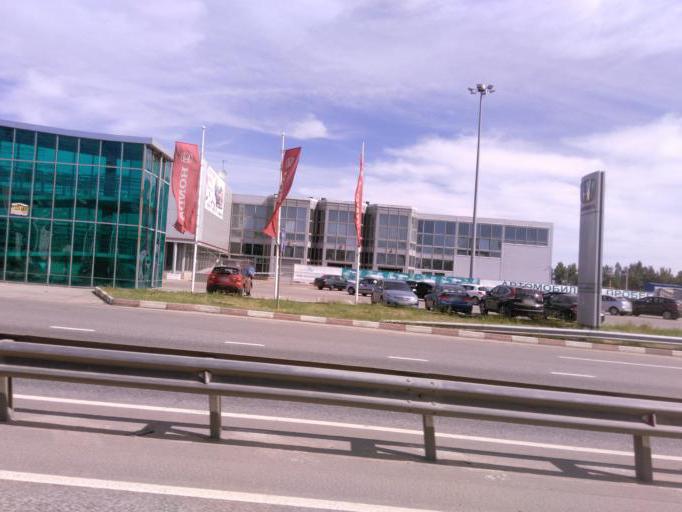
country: RU
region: Moskovskaya
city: Skhodnya
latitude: 55.9744
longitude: 37.3119
